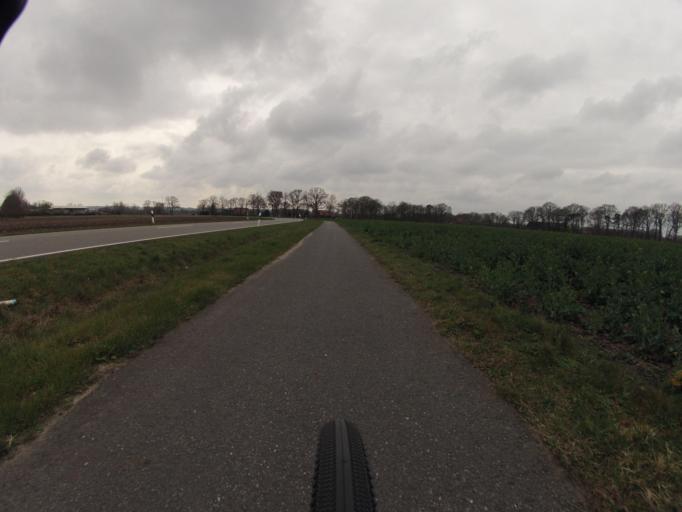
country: DE
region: North Rhine-Westphalia
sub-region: Regierungsbezirk Munster
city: Mettingen
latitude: 52.3433
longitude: 7.7821
